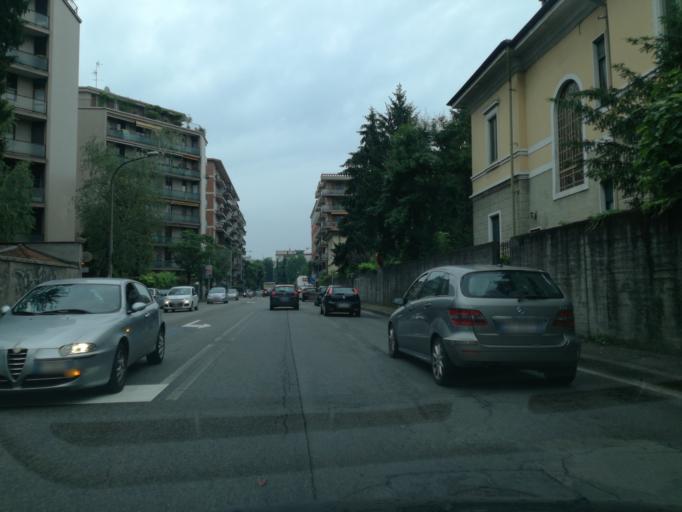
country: IT
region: Lombardy
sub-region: Provincia di Monza e Brianza
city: Monza
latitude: 45.5896
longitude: 9.2830
